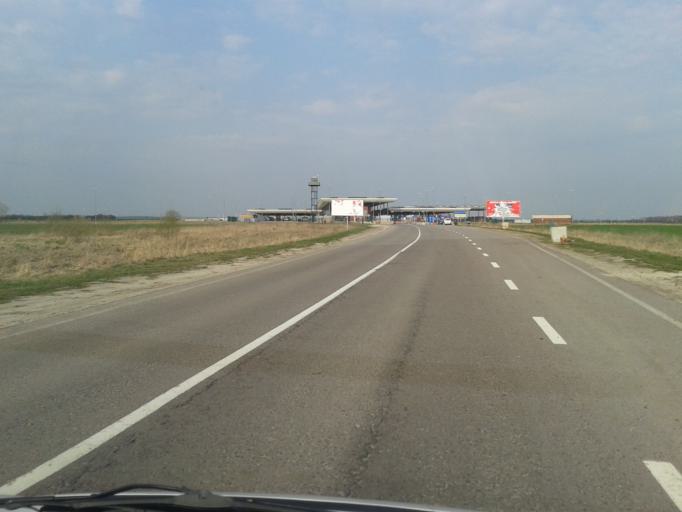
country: PL
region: Lublin Voivodeship
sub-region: Powiat hrubieszowski
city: Dolhobyczow
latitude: 50.5777
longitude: 24.0942
